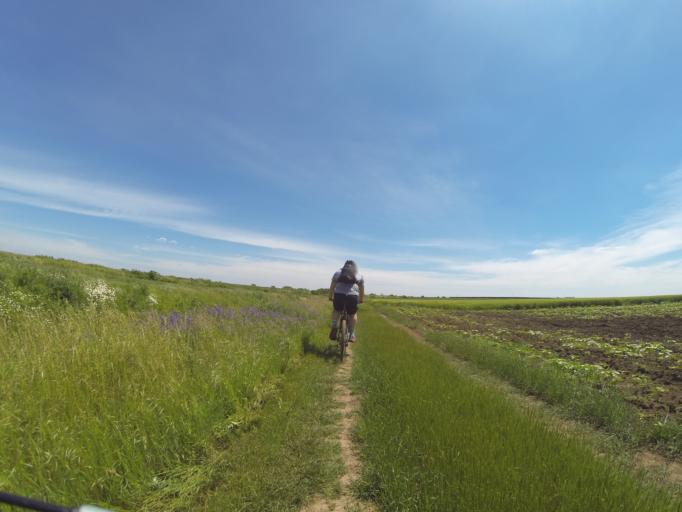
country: RO
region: Dolj
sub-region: Comuna Leu
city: Zanoaga
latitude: 44.1829
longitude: 24.0696
